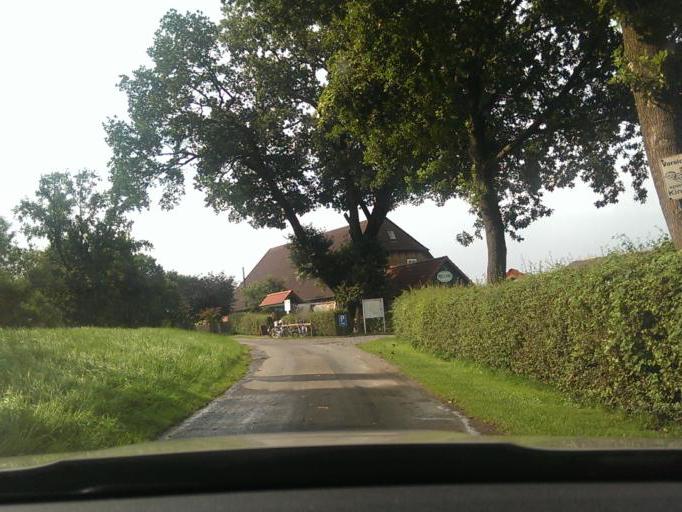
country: DE
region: Lower Saxony
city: Ritterhude
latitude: 53.1625
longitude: 8.7659
